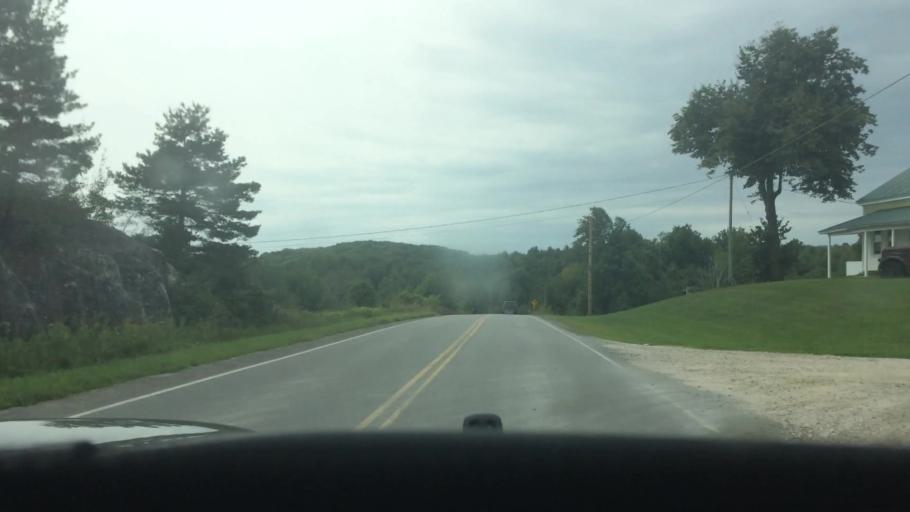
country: US
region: New York
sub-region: St. Lawrence County
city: Canton
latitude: 44.4878
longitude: -75.2488
